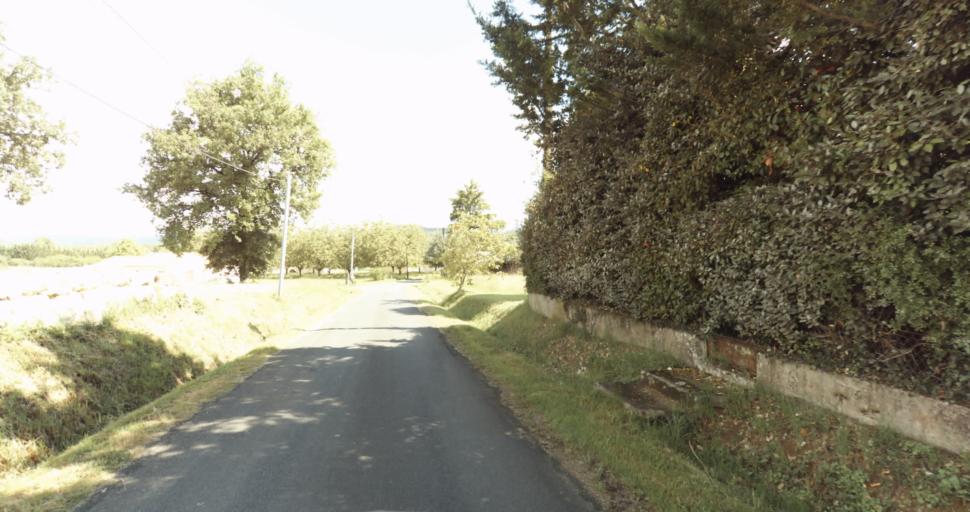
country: FR
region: Aquitaine
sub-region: Departement de la Dordogne
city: Le Bugue
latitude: 44.8438
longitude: 0.9014
